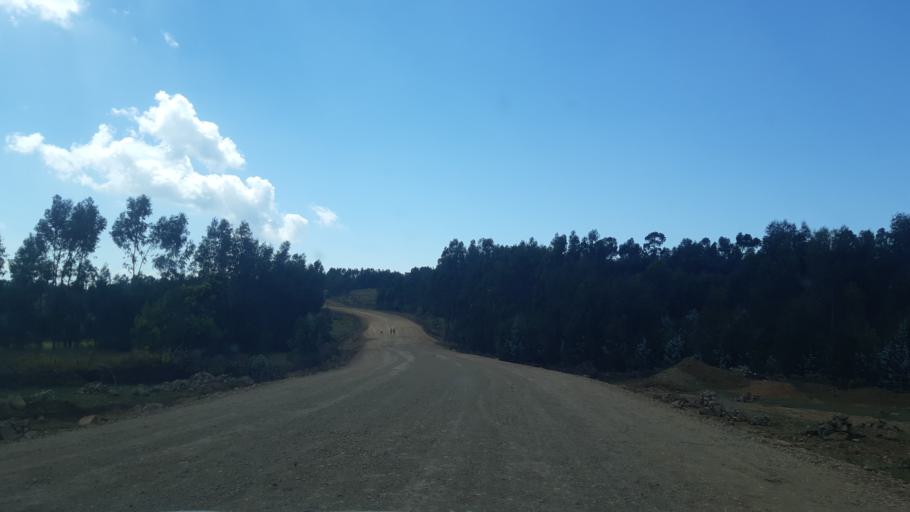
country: ET
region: Amhara
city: Dabat
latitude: 13.3667
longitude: 37.3835
